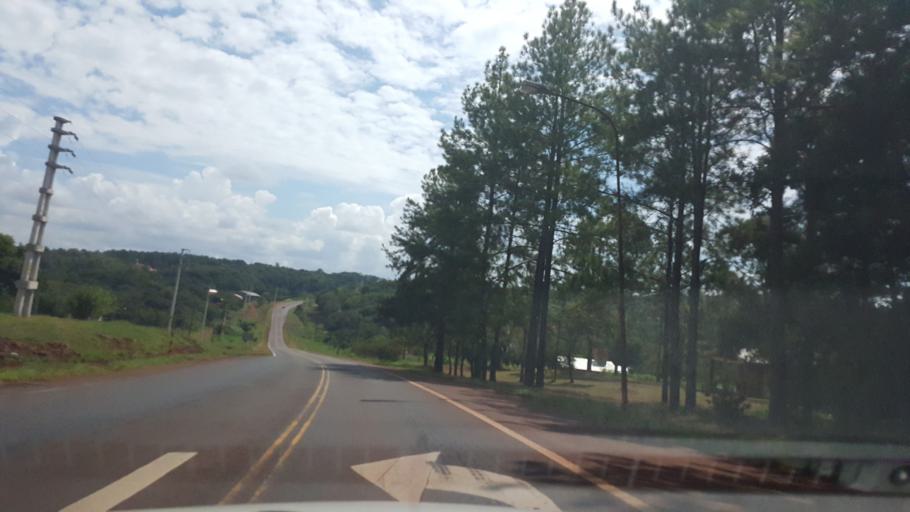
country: AR
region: Misiones
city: Capiovi
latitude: -26.8647
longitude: -55.0450
